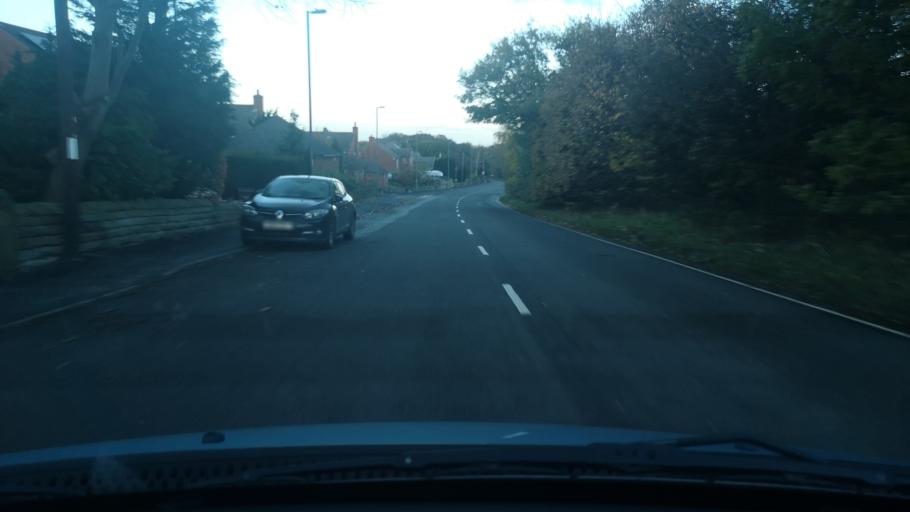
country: GB
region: England
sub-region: City and Borough of Wakefield
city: Middlestown
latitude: 53.6295
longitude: -1.5895
